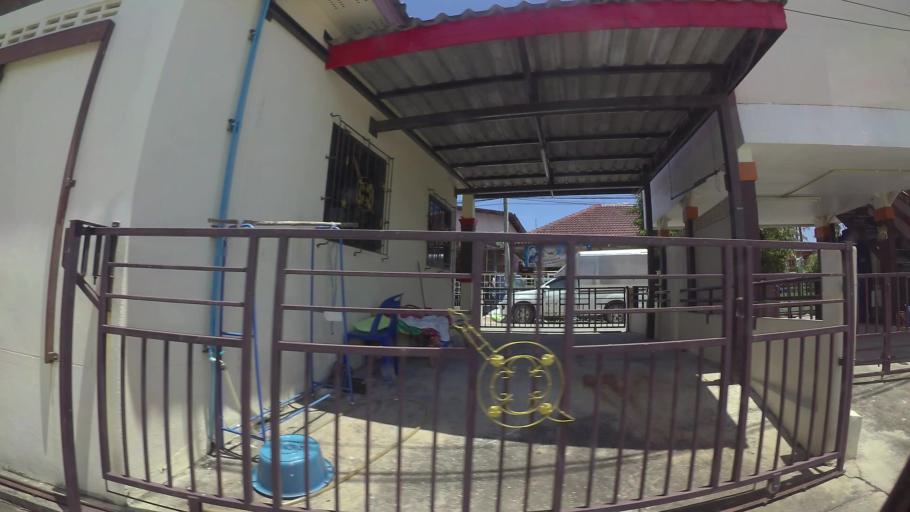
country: TH
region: Chon Buri
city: Si Racha
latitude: 13.1184
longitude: 100.9421
